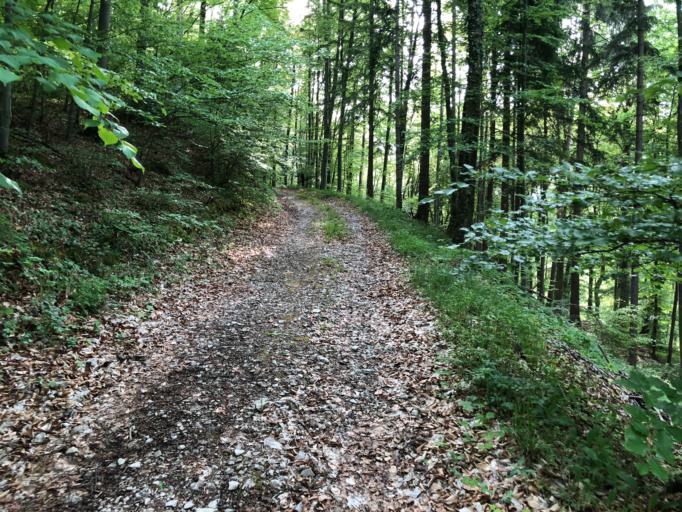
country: DE
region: Baden-Wuerttemberg
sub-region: Tuebingen Region
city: Mossingen
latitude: 48.3888
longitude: 9.0815
